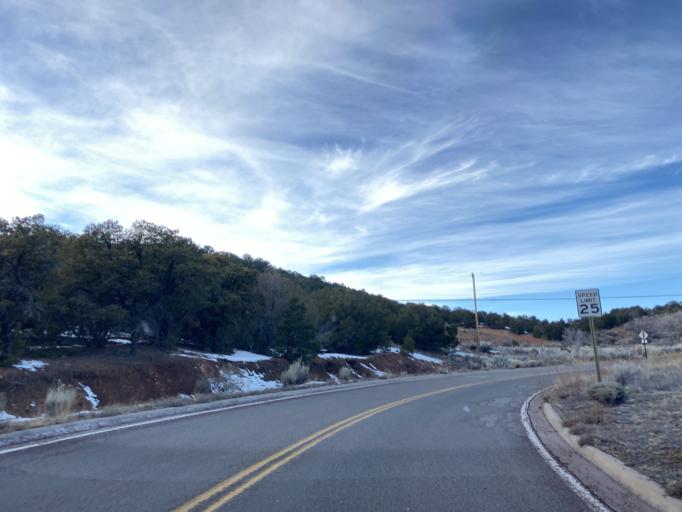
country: US
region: New Mexico
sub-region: Santa Fe County
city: Santa Fe
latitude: 35.7099
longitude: -105.8995
